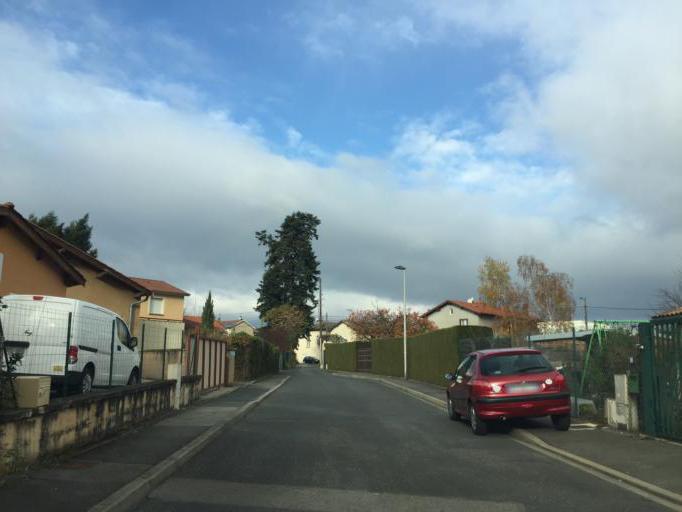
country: FR
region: Rhone-Alpes
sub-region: Departement du Rhone
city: Villefranche-sur-Saone
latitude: 45.9988
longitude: 4.7247
